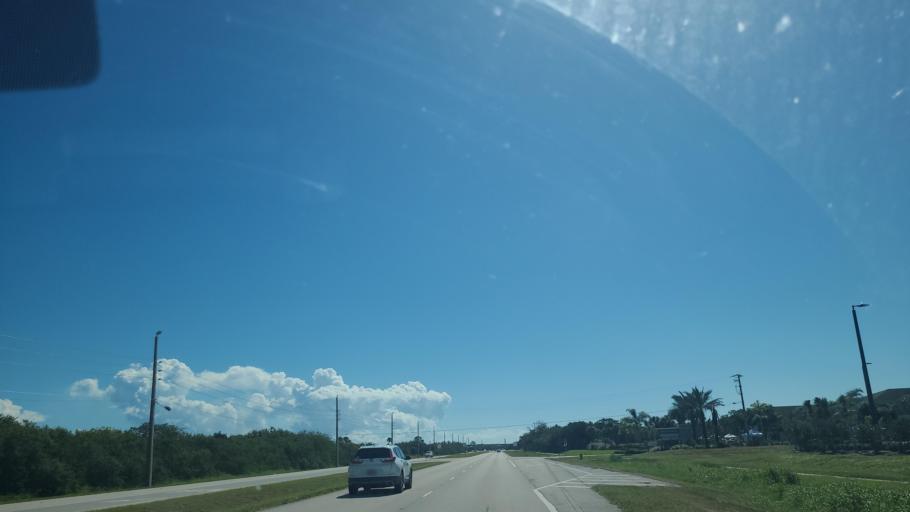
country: US
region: Florida
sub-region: Indian River County
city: Gifford
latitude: 27.6641
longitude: -80.3915
